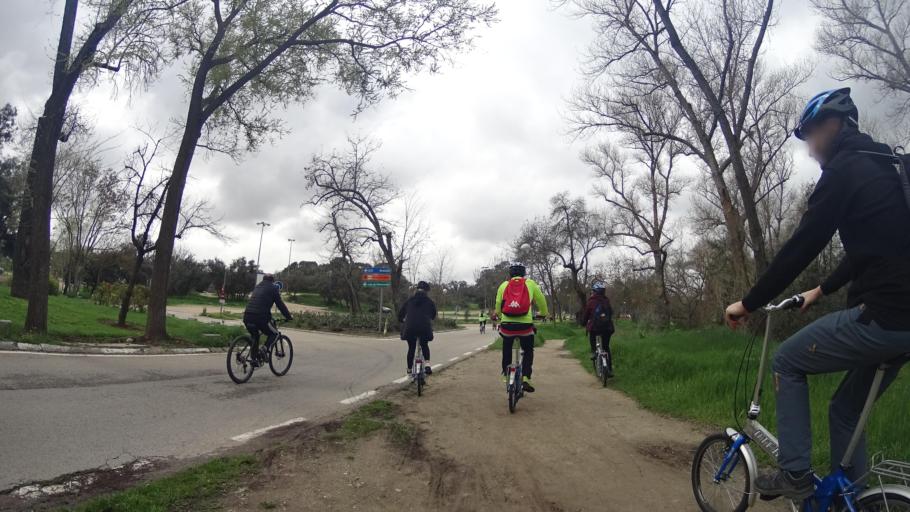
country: ES
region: Madrid
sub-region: Provincia de Madrid
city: Latina
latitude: 40.4122
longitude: -3.7546
